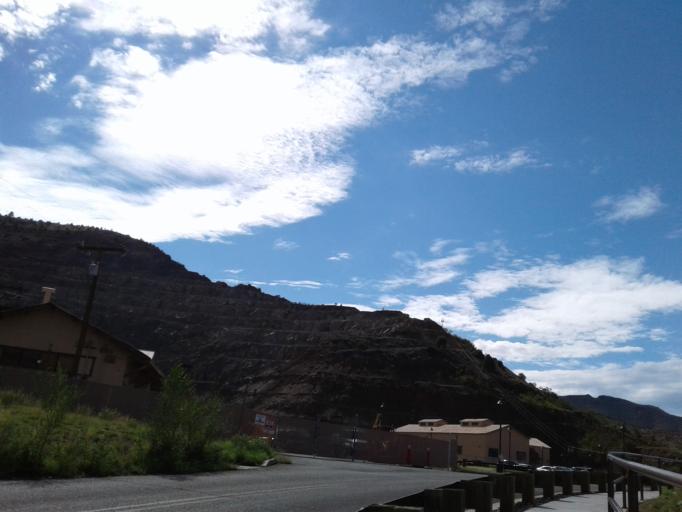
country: US
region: Arizona
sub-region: Yavapai County
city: Clarkdale
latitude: 34.7527
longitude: -112.1192
